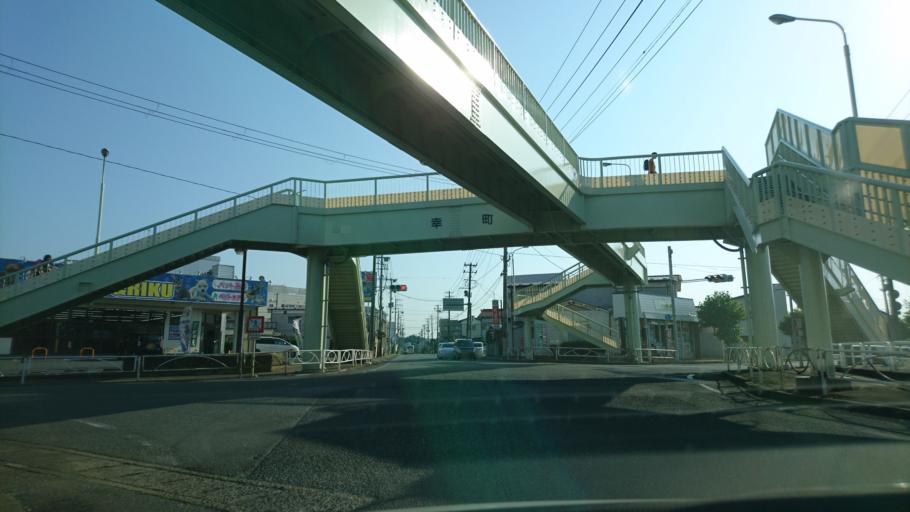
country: JP
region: Iwate
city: Ichinoseki
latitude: 38.9311
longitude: 141.1225
